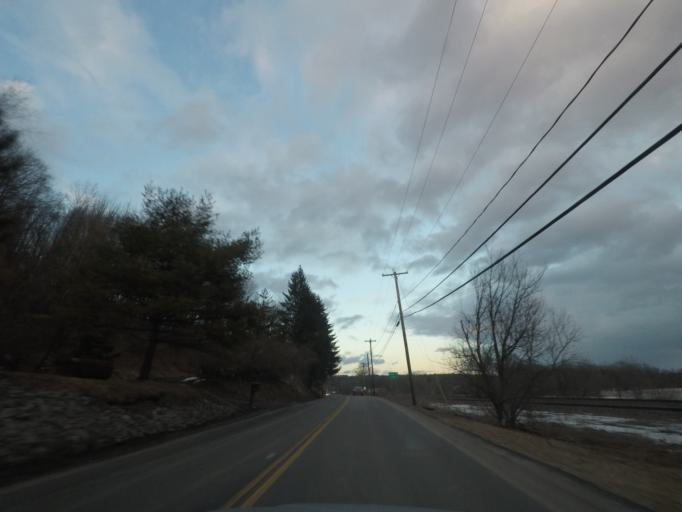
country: US
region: New York
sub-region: Montgomery County
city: Fonda
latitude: 42.9523
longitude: -74.3846
